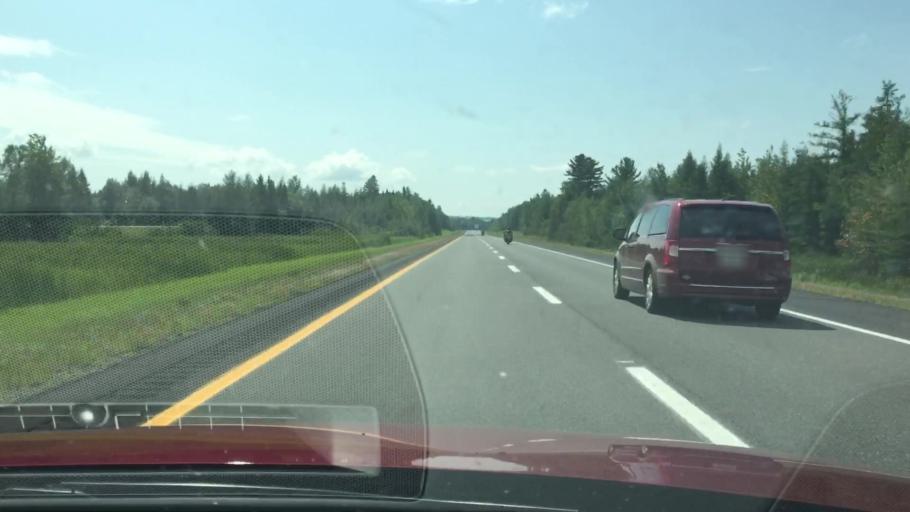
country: US
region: Maine
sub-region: Penobscot County
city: Patten
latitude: 45.9828
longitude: -68.2881
